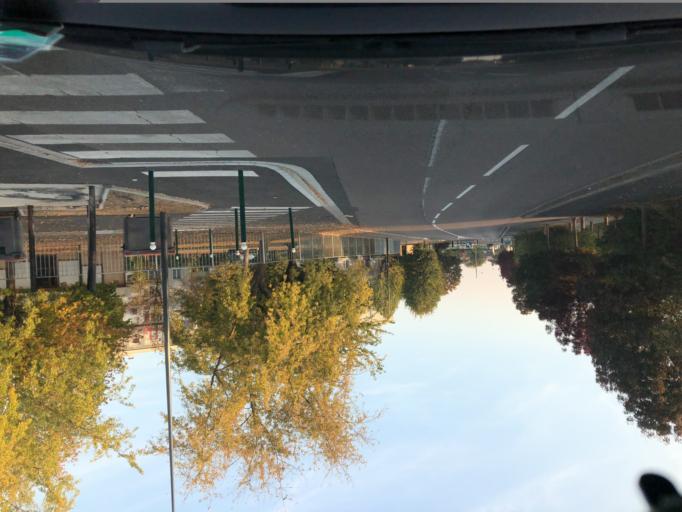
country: FR
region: Bourgogne
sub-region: Departement de l'Yonne
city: Sens
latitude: 48.1990
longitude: 3.3027
